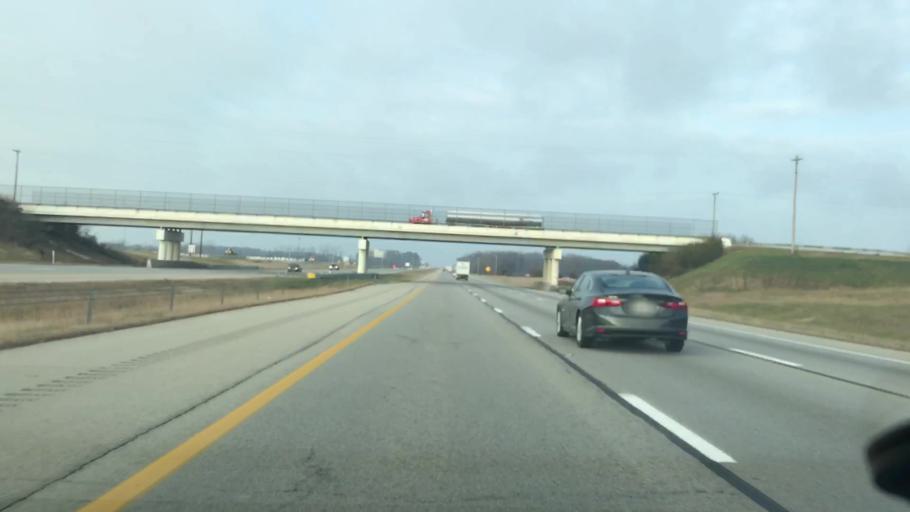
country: US
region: Ohio
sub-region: Clark County
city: Lisbon
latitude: 39.9330
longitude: -83.6107
